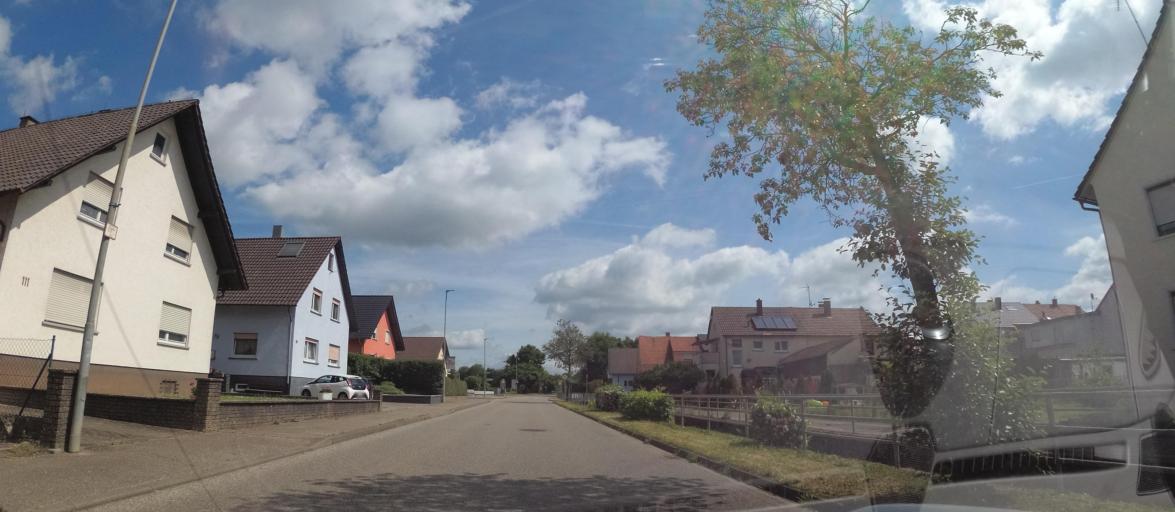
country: DE
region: Baden-Wuerttemberg
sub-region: Karlsruhe Region
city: Gondelsheim
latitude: 49.0753
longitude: 8.6867
